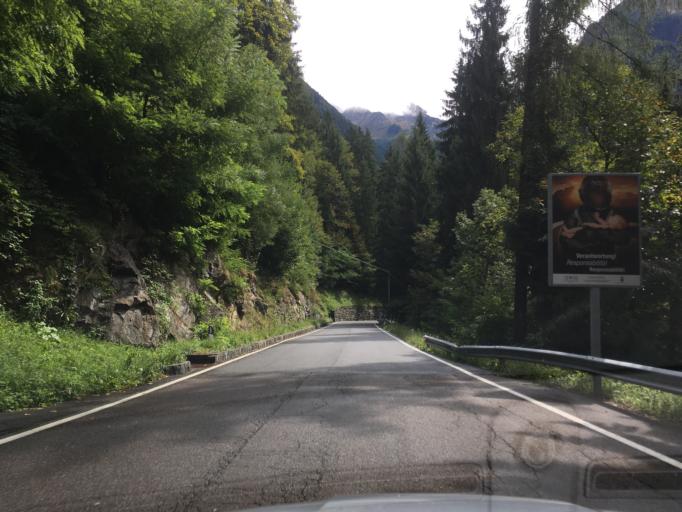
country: IT
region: Trentino-Alto Adige
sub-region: Bolzano
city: San Leonardo in Passiria
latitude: 46.8183
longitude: 11.2483
